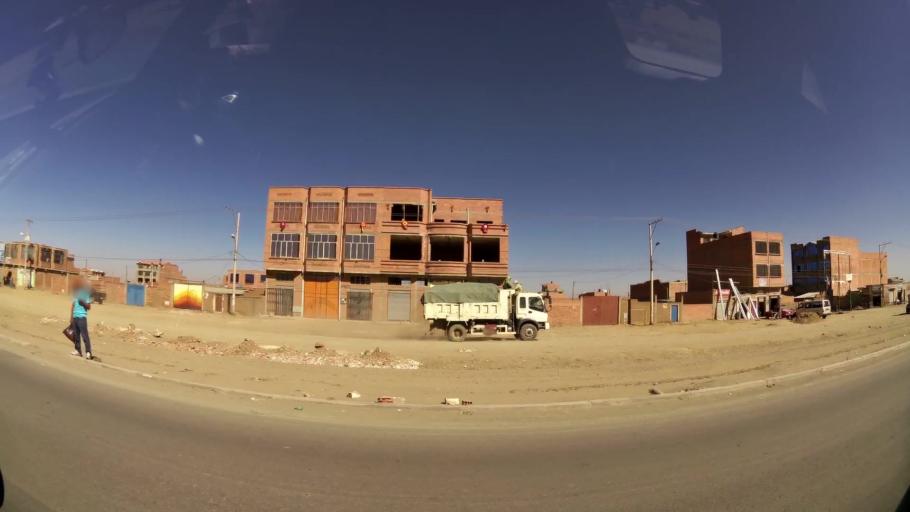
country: BO
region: La Paz
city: La Paz
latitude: -16.6125
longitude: -68.1829
